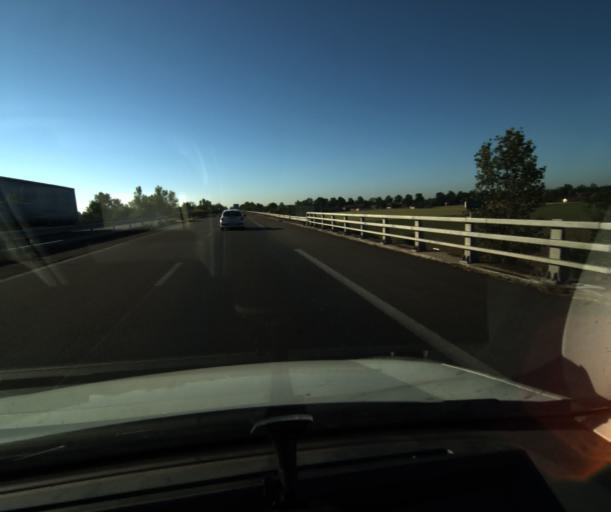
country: FR
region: Midi-Pyrenees
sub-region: Departement du Tarn-et-Garonne
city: Saint-Porquier
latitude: 44.0370
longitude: 1.1547
